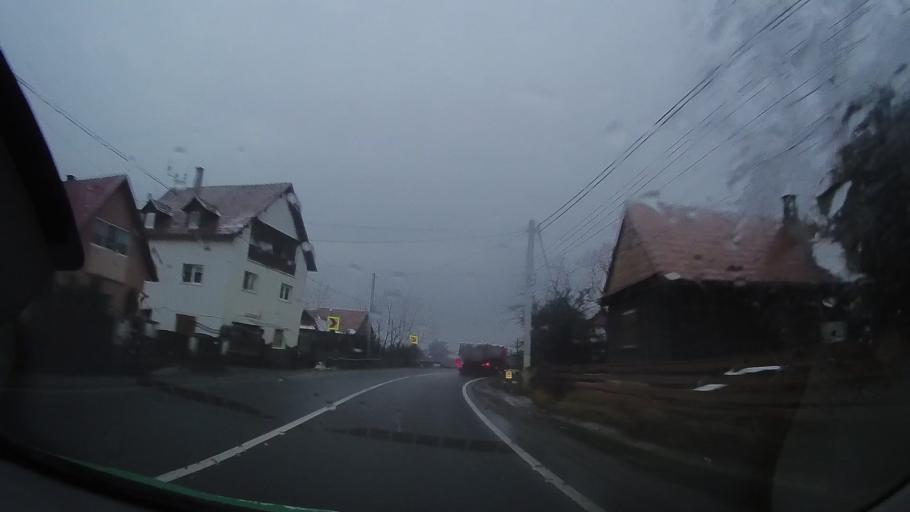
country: RO
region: Harghita
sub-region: Comuna Lazarea
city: Lazarea
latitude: 46.7527
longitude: 25.5197
